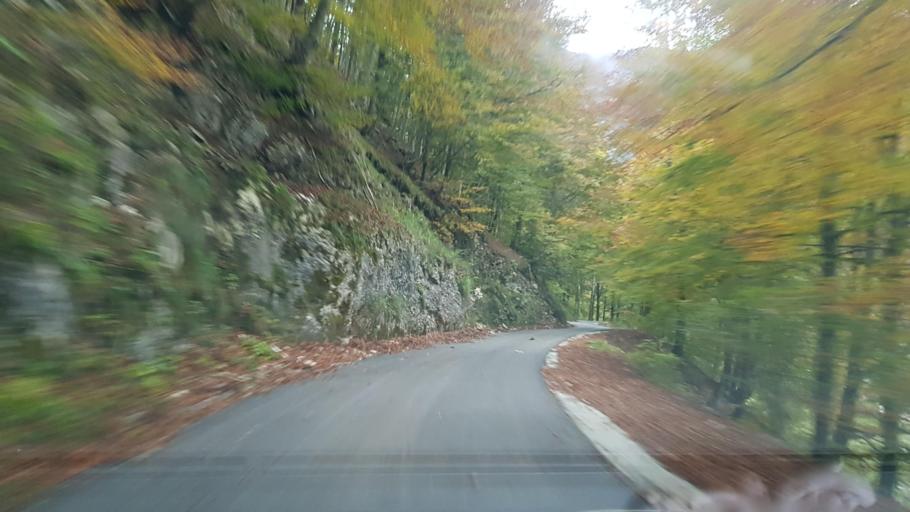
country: IT
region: Friuli Venezia Giulia
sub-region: Provincia di Udine
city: Preone
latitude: 46.3431
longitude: 12.8834
